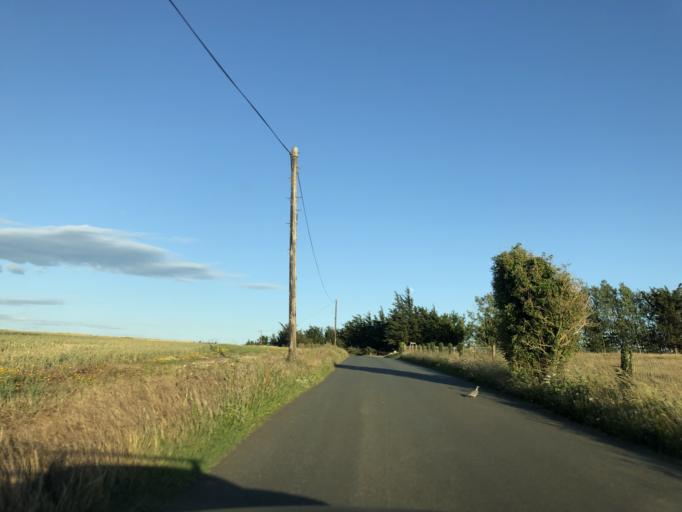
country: GB
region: England
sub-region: Isle of Wight
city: Chale
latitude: 50.6360
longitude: -1.3340
